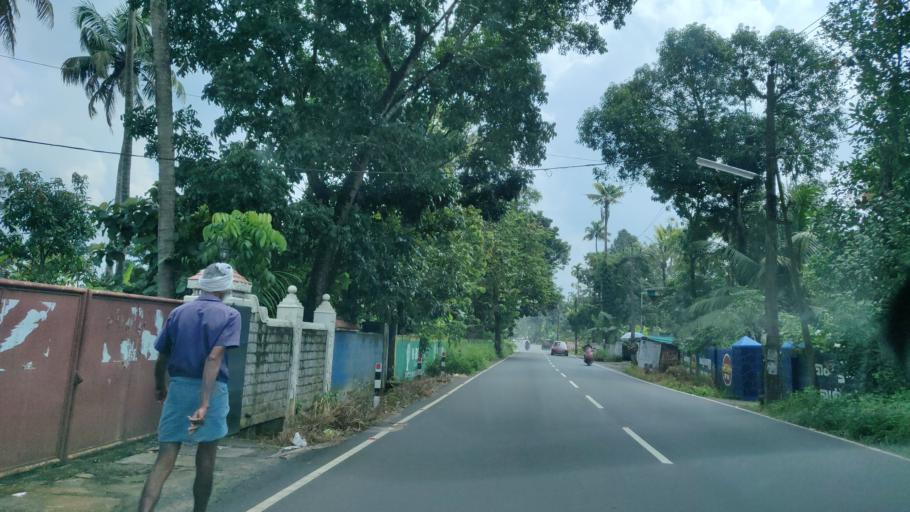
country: IN
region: Kerala
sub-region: Ernakulam
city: Angamali
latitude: 10.1675
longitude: 76.4185
